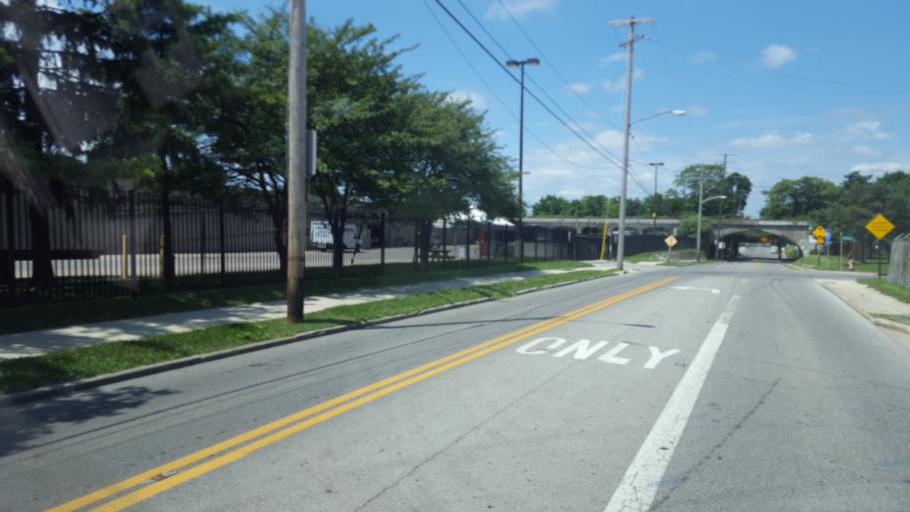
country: US
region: Ohio
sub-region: Franklin County
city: Columbus
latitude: 40.0011
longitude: -82.9934
